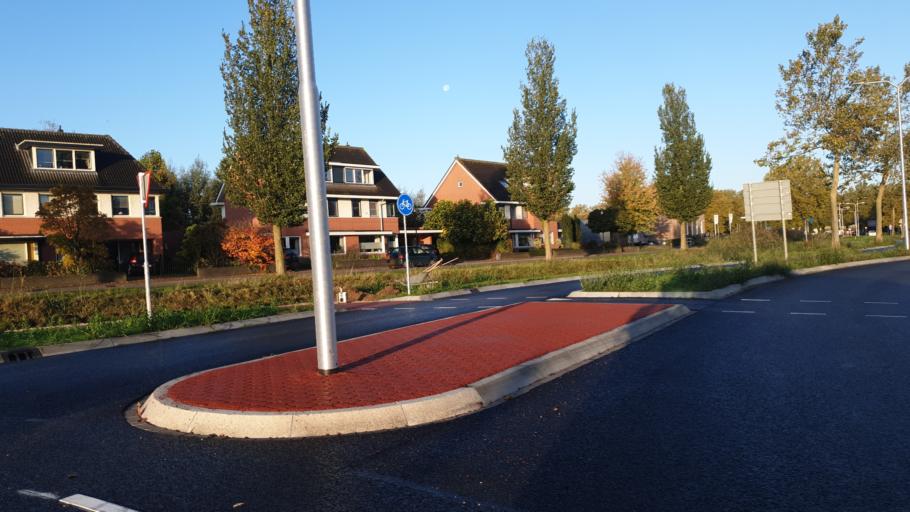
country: NL
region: Gelderland
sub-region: Gemeente Druten
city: Druten
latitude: 51.8832
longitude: 5.6086
